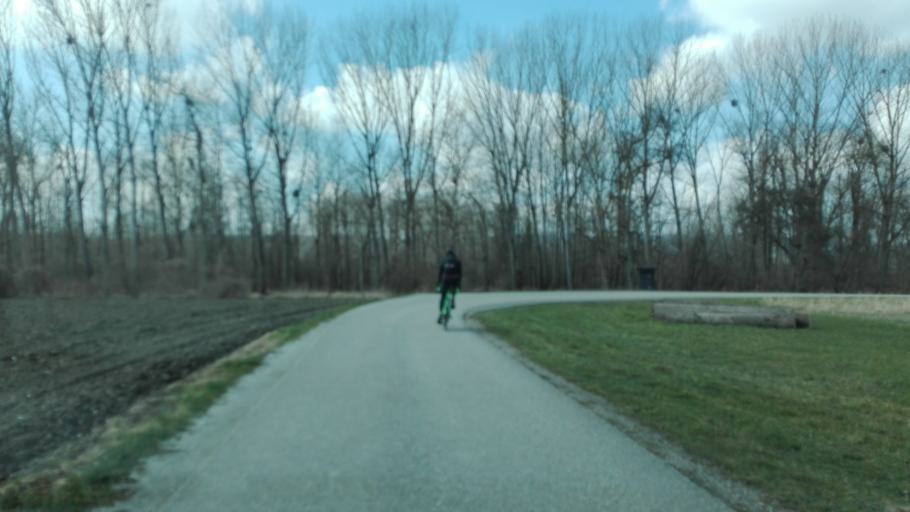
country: AT
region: Upper Austria
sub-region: Politischer Bezirk Urfahr-Umgebung
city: Feldkirchen an der Donau
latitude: 48.3433
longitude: 14.0318
